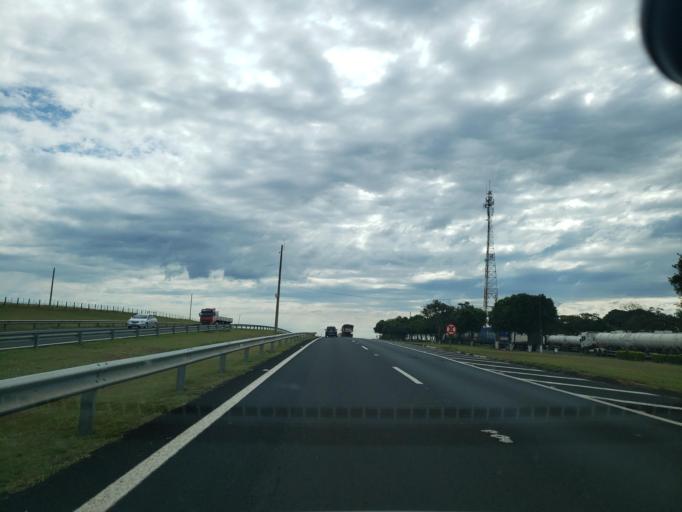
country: BR
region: Sao Paulo
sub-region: Bauru
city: Bauru
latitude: -22.1873
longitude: -49.2116
